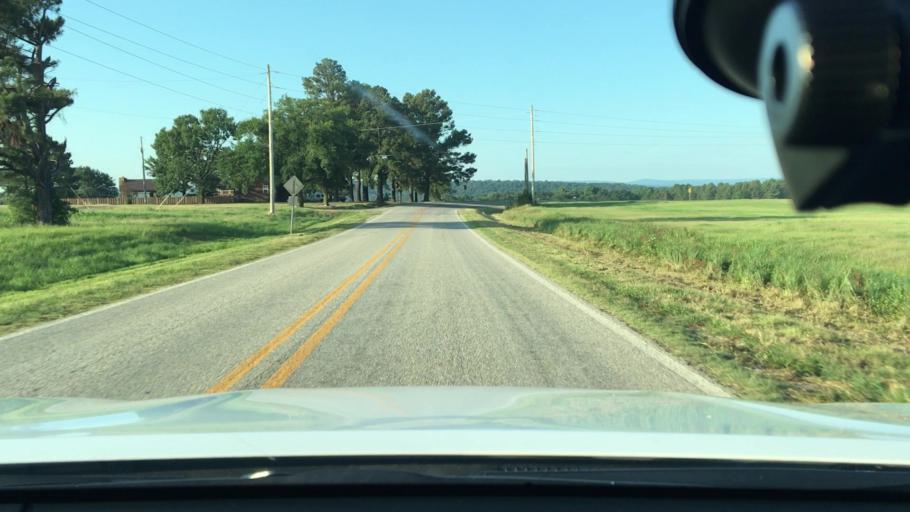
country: US
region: Arkansas
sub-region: Johnson County
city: Coal Hill
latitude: 35.3492
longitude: -93.5886
